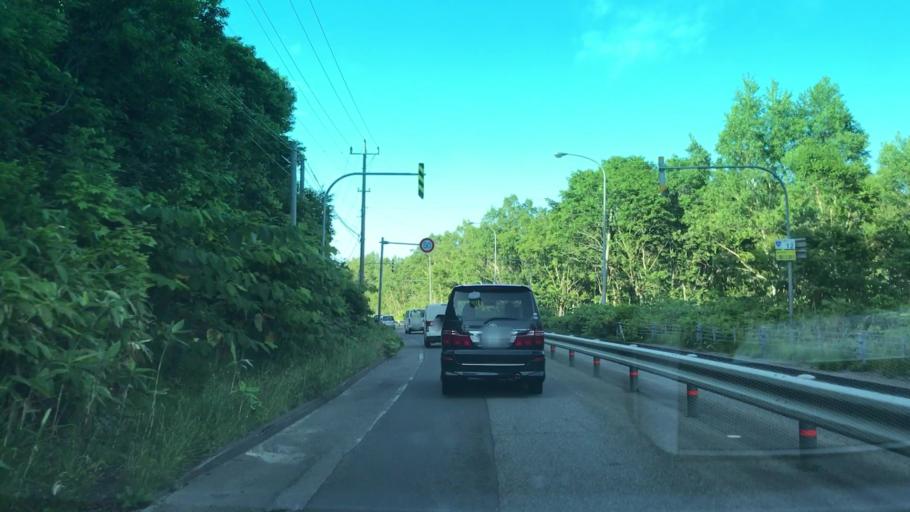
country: JP
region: Hokkaido
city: Otaru
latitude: 43.1346
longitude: 141.0127
